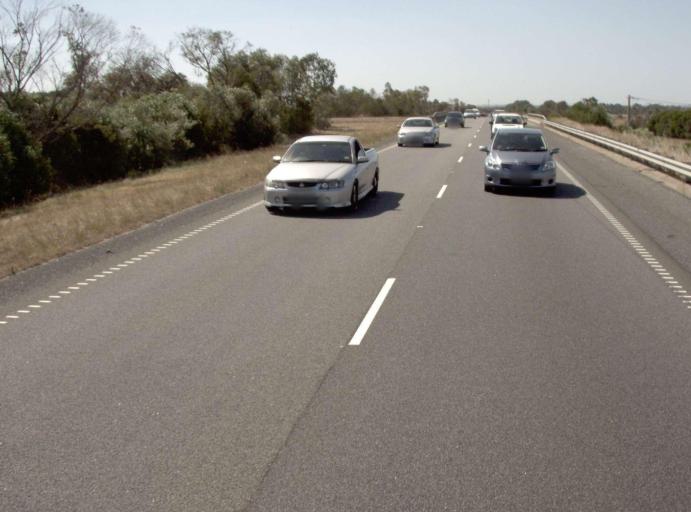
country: AU
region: Victoria
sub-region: Kingston
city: Chelsea Heights
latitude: -38.0444
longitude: 145.1422
